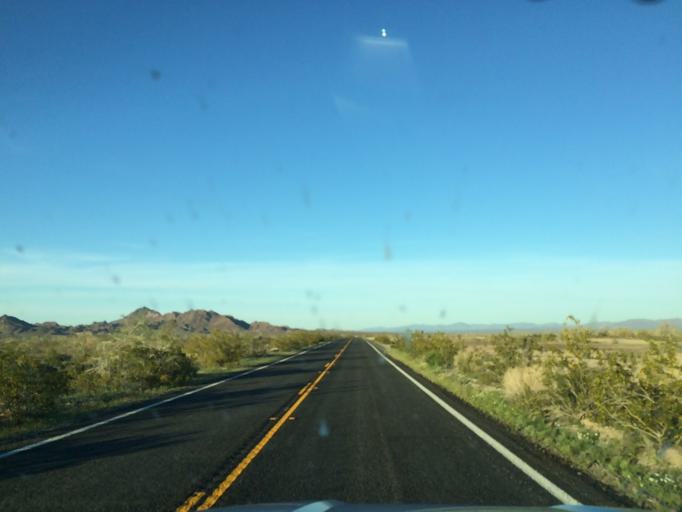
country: US
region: California
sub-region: Riverside County
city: Mesa Verde
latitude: 33.2573
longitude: -114.8096
